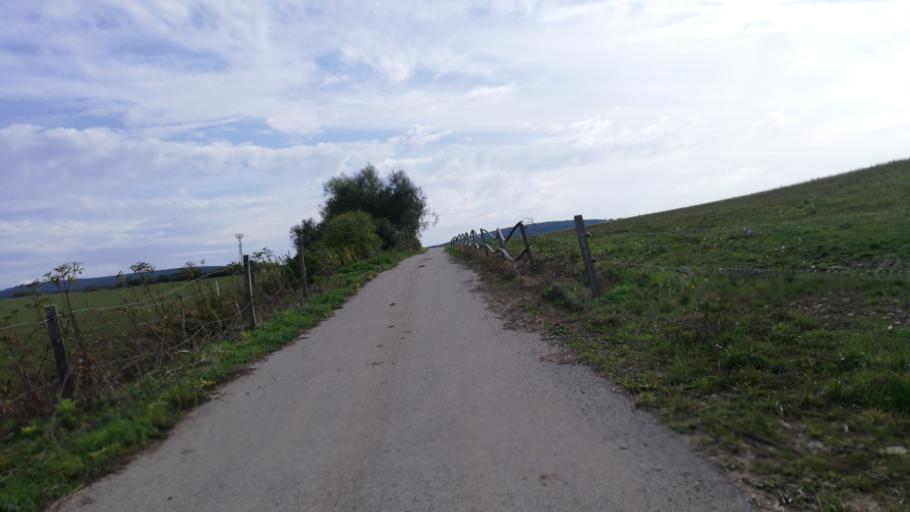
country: CZ
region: South Moravian
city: Sudomerice
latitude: 48.8421
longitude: 17.2822
